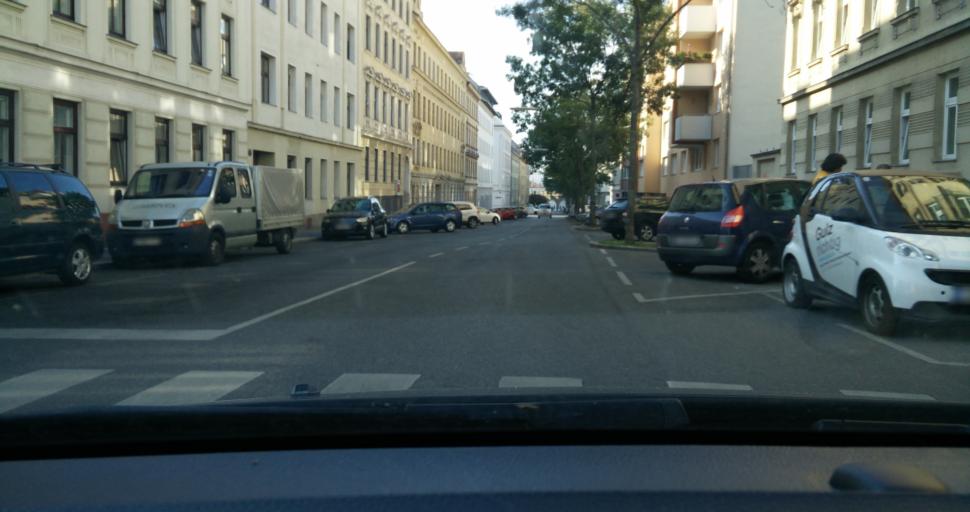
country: AT
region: Vienna
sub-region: Wien Stadt
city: Vienna
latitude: 48.2172
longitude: 16.3115
